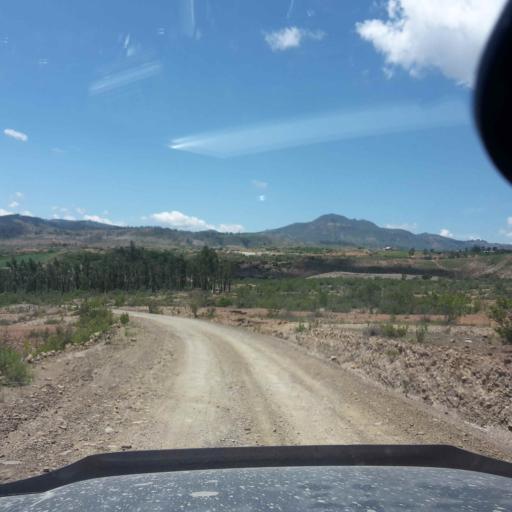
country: BO
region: Cochabamba
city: Totora
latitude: -17.7720
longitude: -65.2668
